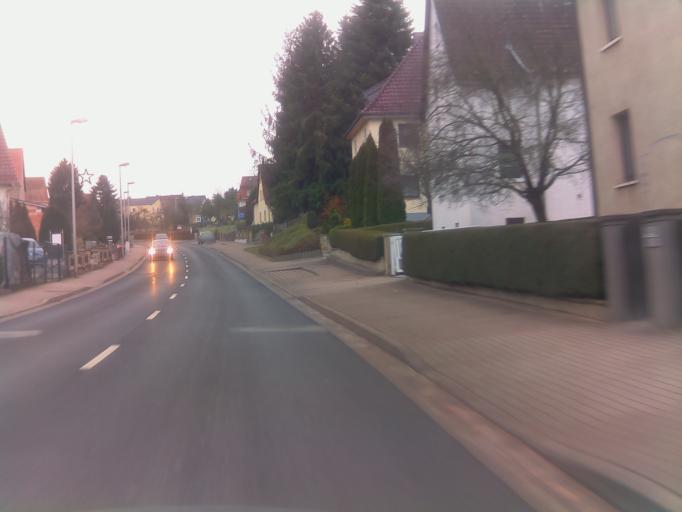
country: DE
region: Thuringia
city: Unterbreizbach
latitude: 50.7943
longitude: 9.9984
